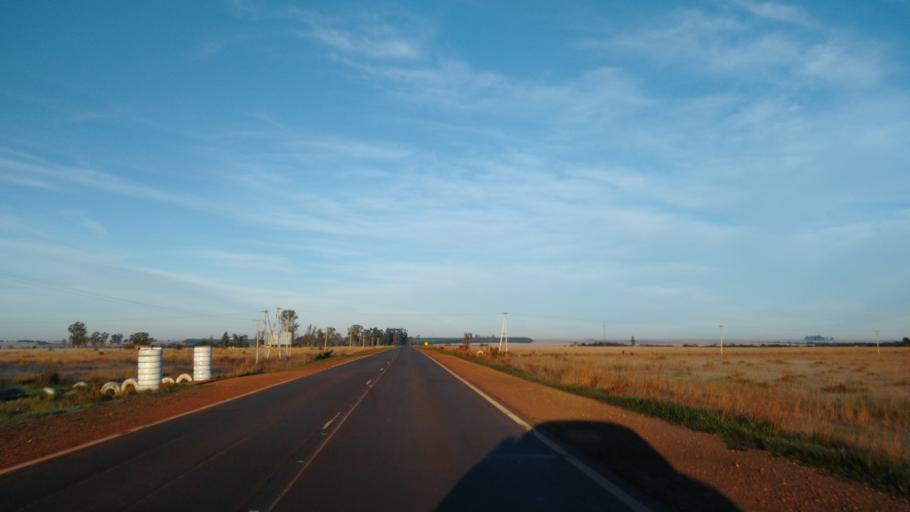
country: AR
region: Corrientes
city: Santo Tome
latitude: -28.5890
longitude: -56.0922
